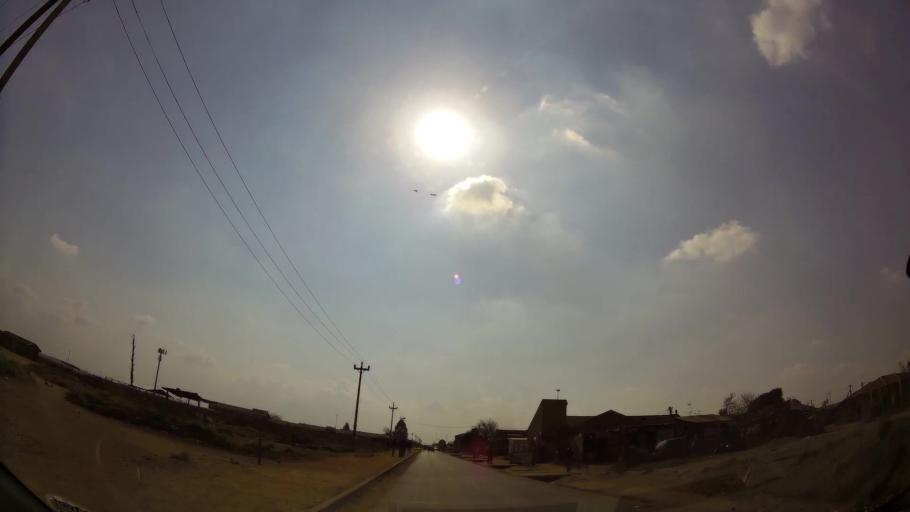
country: ZA
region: Gauteng
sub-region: Ekurhuleni Metropolitan Municipality
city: Springs
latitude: -26.1192
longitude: 28.4795
